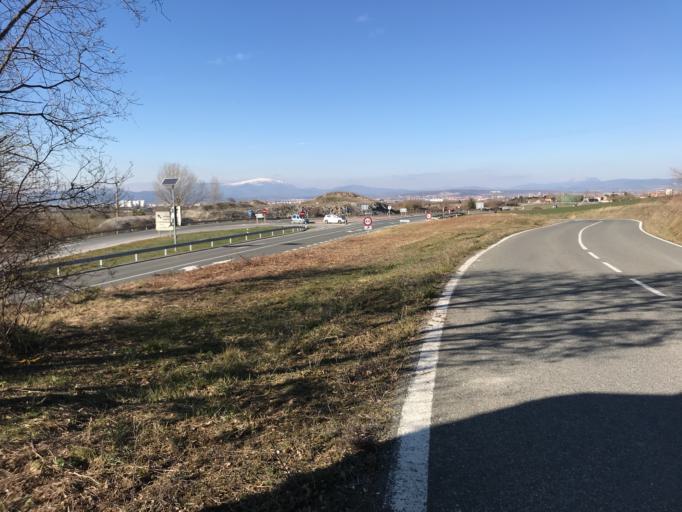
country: ES
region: Basque Country
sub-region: Provincia de Alava
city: Gasteiz / Vitoria
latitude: 42.8135
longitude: -2.6806
